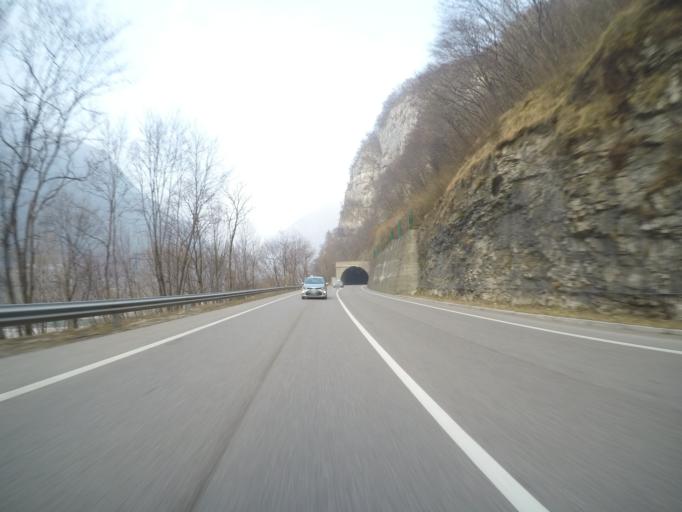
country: IT
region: Veneto
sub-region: Provincia di Belluno
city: Vas
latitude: 45.9481
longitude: 11.9285
